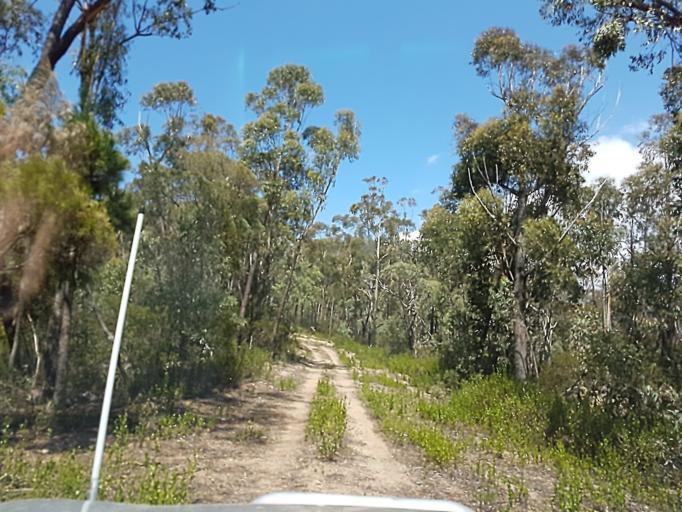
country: AU
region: Victoria
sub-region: East Gippsland
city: Lakes Entrance
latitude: -37.3068
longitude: 148.3610
